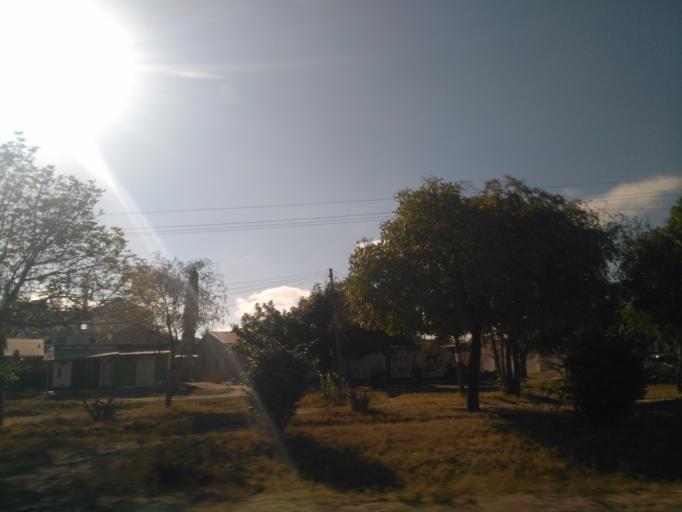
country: TZ
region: Dodoma
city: Dodoma
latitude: -6.1640
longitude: 35.7464
